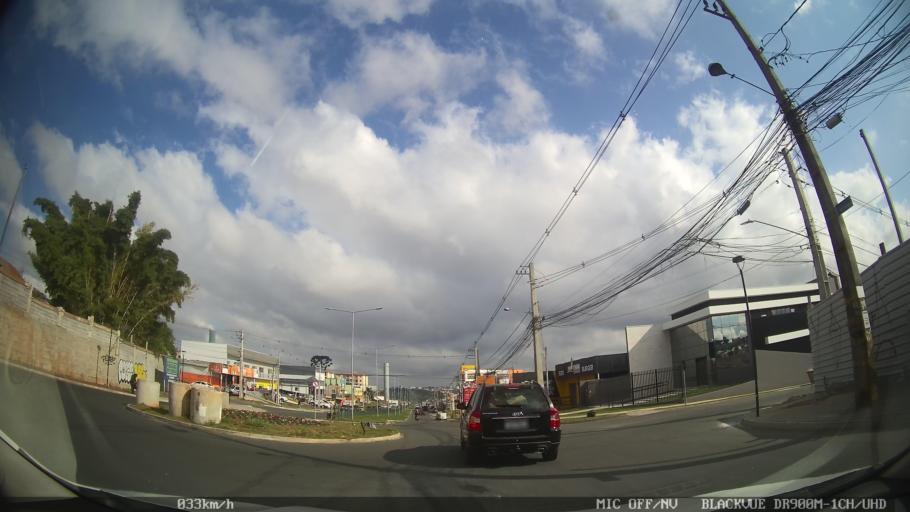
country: BR
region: Parana
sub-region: Pinhais
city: Pinhais
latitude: -25.3831
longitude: -49.1863
